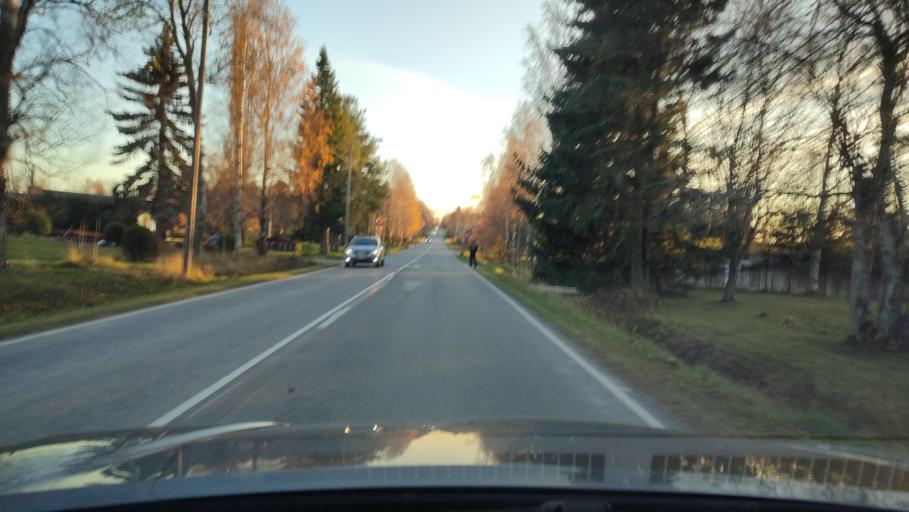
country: FI
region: Ostrobothnia
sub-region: Sydosterbotten
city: Naerpes
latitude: 62.4944
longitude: 21.3433
